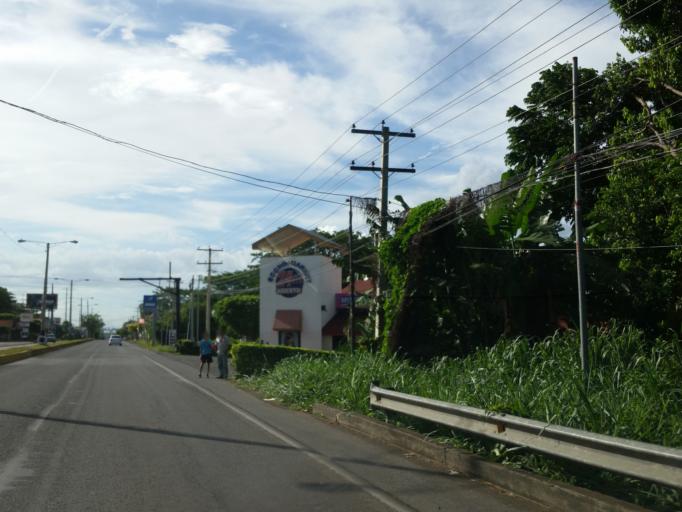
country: NI
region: Masaya
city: Ticuantepe
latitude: 12.0462
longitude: -86.1943
